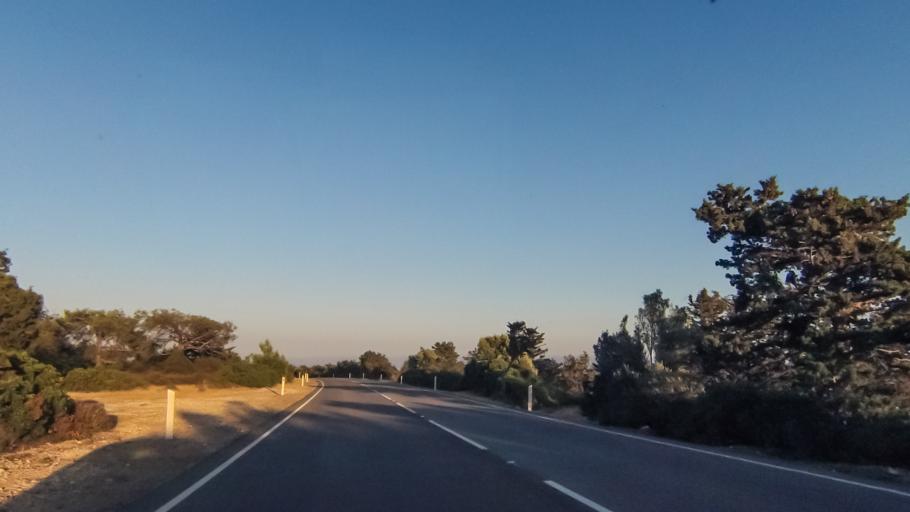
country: CY
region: Limassol
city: Sotira
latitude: 34.6720
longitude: 32.8572
